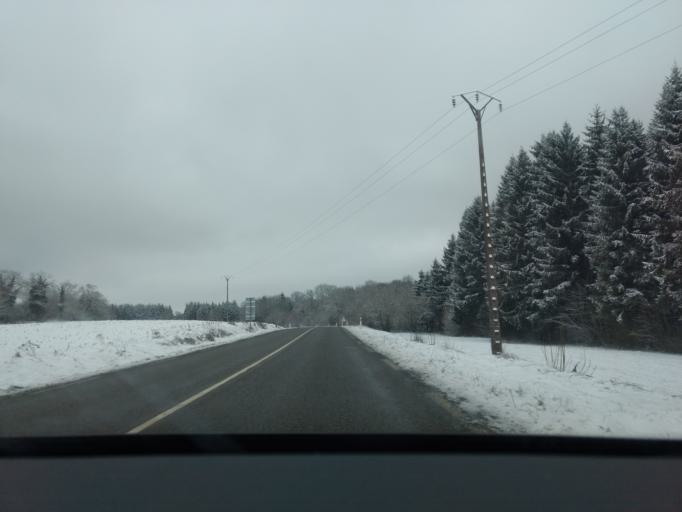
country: FR
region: Franche-Comte
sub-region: Departement du Jura
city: Champagnole
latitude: 46.7856
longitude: 5.8547
